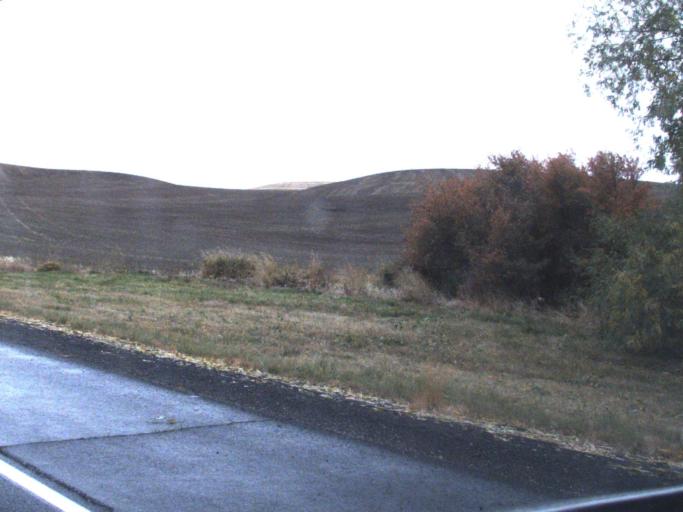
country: US
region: Washington
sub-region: Whitman County
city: Pullman
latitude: 46.7406
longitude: -117.2306
